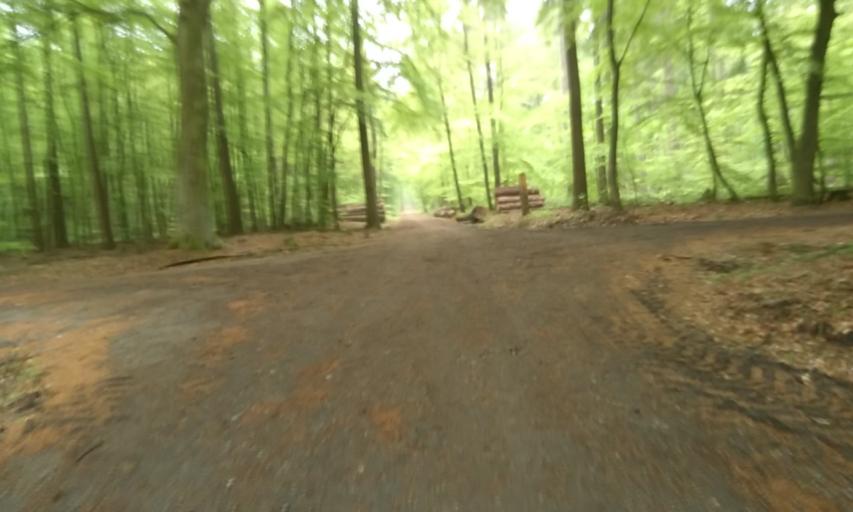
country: DE
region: Lower Saxony
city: Nottensdorf
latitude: 53.4707
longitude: 9.6405
